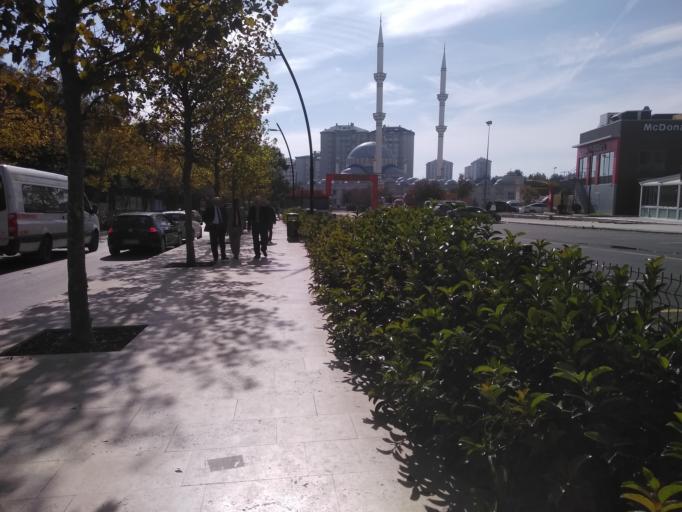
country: TR
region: Istanbul
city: Beylikduezue
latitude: 41.0112
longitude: 28.6439
